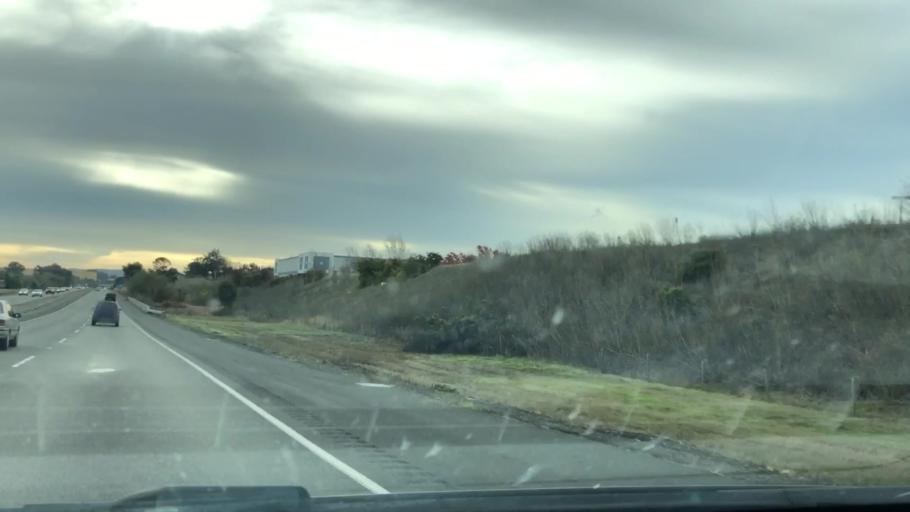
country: US
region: California
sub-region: Solano County
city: Benicia
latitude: 38.0775
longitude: -122.1203
